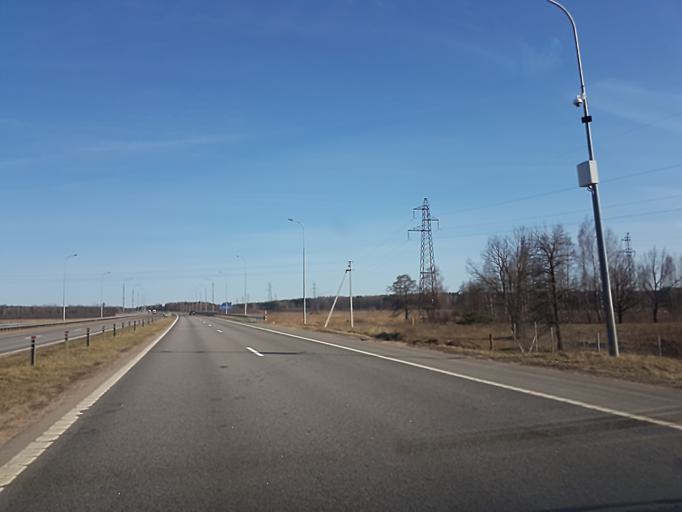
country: BY
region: Mogilev
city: Asipovichy
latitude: 53.4132
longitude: 28.4760
